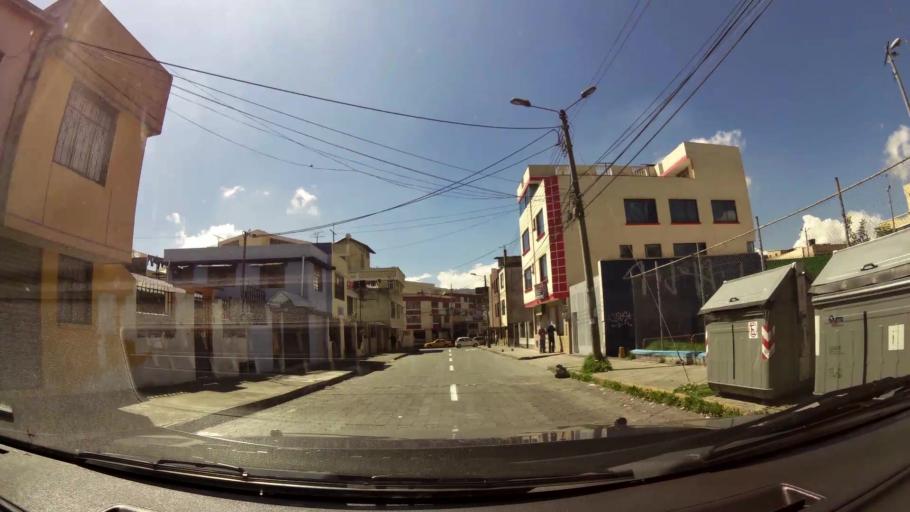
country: EC
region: Pichincha
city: Quito
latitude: -0.2549
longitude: -78.5350
